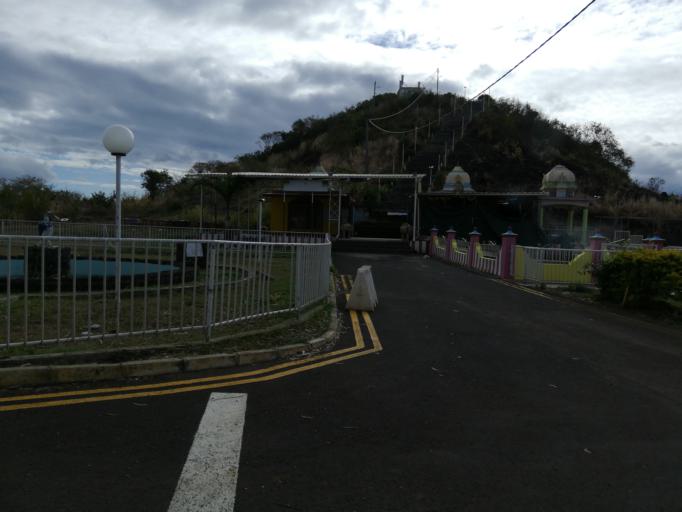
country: MU
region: Black River
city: Gros Cailloux
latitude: -20.2286
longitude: 57.4515
